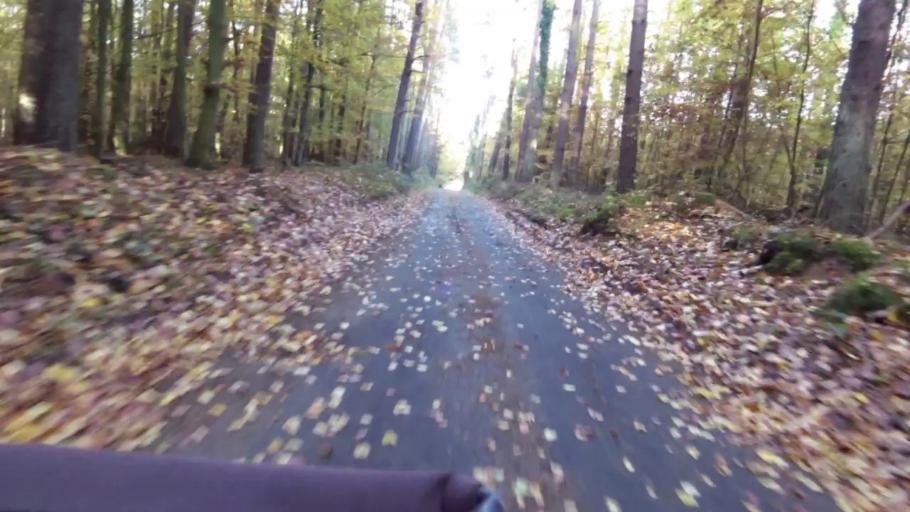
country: PL
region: West Pomeranian Voivodeship
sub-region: Powiat kamienski
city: Wolin
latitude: 53.8653
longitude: 14.5296
